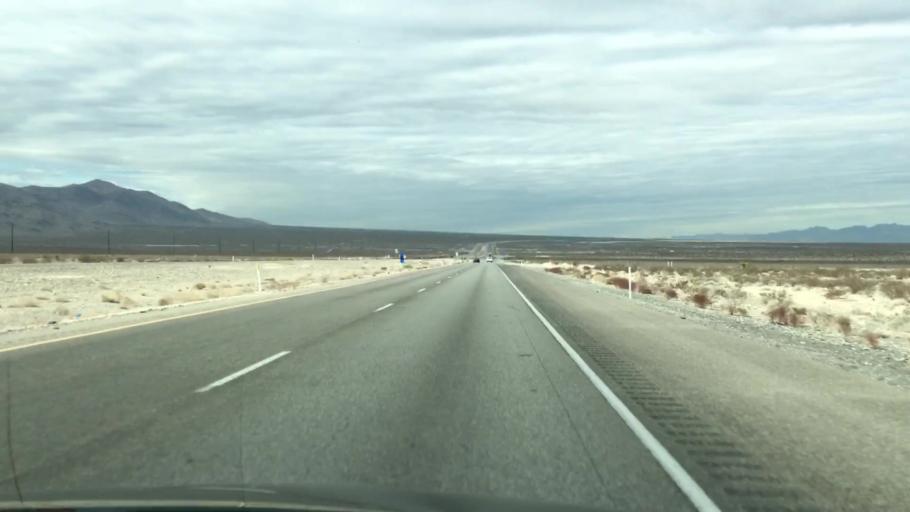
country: US
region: Nevada
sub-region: Clark County
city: Summerlin South
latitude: 36.3951
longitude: -115.3909
